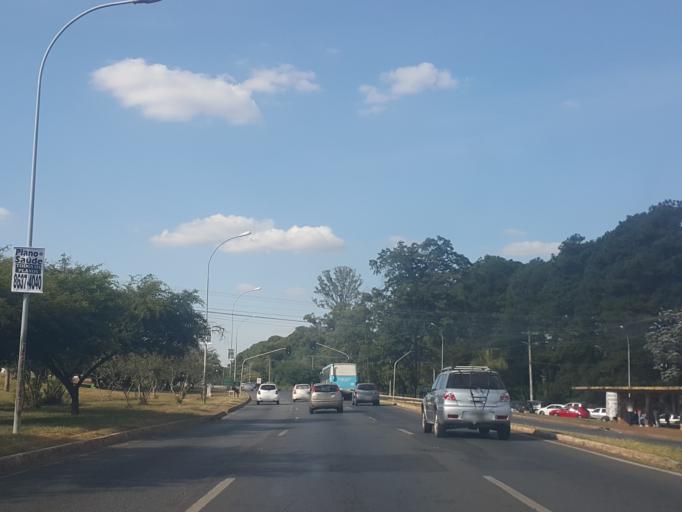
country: BR
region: Federal District
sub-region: Brasilia
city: Brasilia
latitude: -15.8072
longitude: -47.9290
